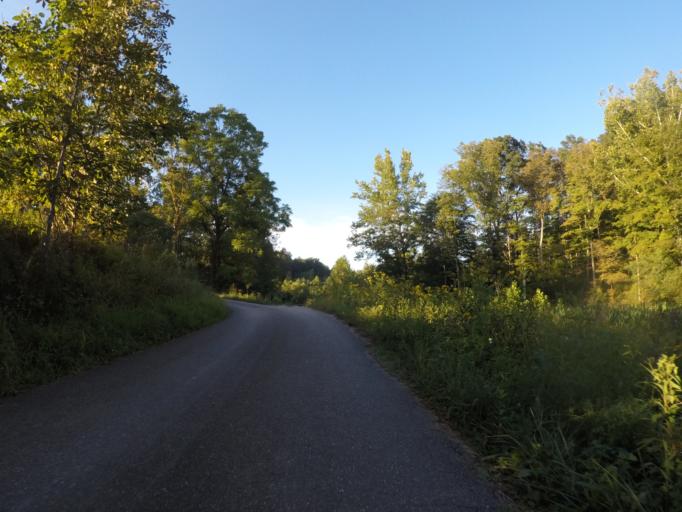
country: US
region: Ohio
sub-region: Lawrence County
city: Coal Grove
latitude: 38.5810
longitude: -82.5461
